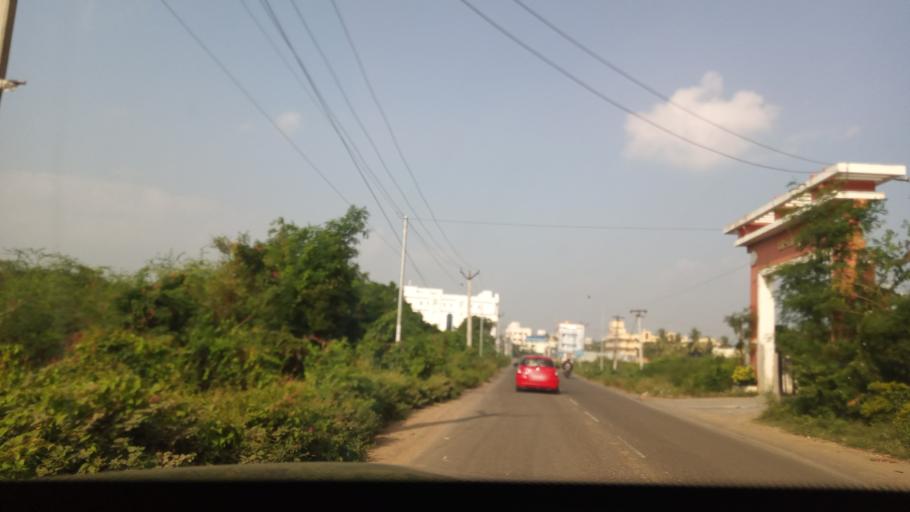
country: IN
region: Tamil Nadu
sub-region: Kancheepuram
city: Vengavasal
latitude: 12.7827
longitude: 80.2265
